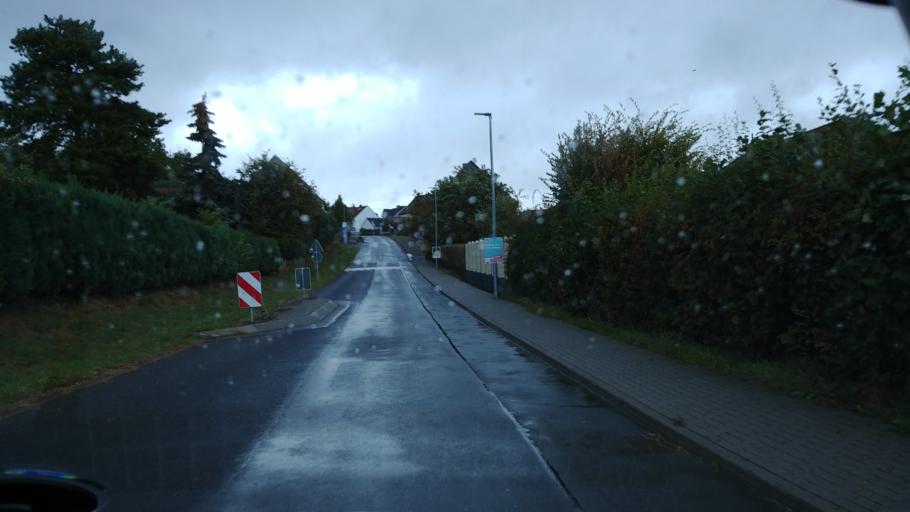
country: DE
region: Hesse
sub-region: Regierungsbezirk Darmstadt
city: Bad Schwalbach
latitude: 50.1565
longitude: 8.1048
